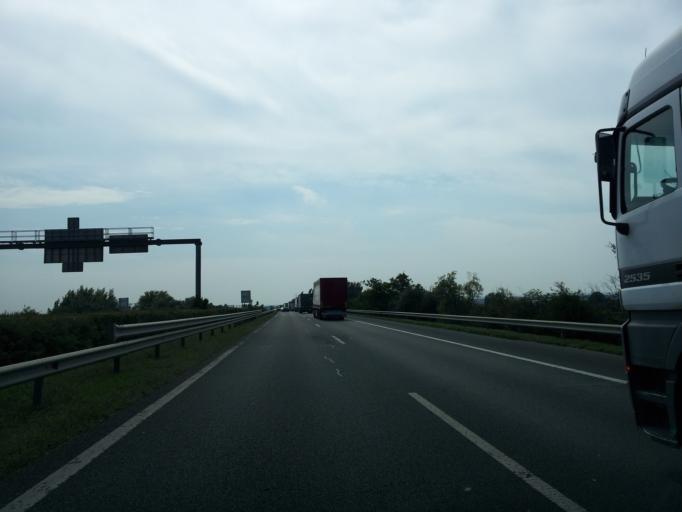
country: HU
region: Fejer
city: Szekesfehervar
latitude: 47.1711
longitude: 18.4652
